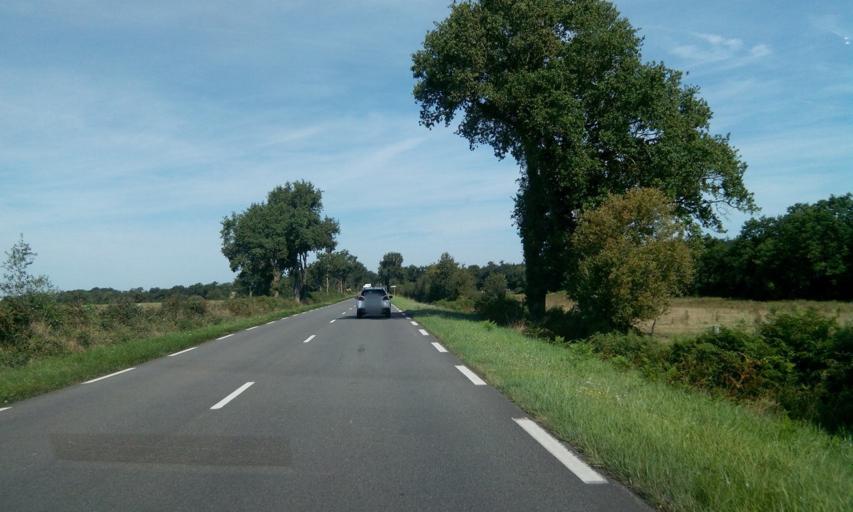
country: FR
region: Poitou-Charentes
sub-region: Departement de la Vienne
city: Availles-Limouzine
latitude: 46.0663
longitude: 0.5990
